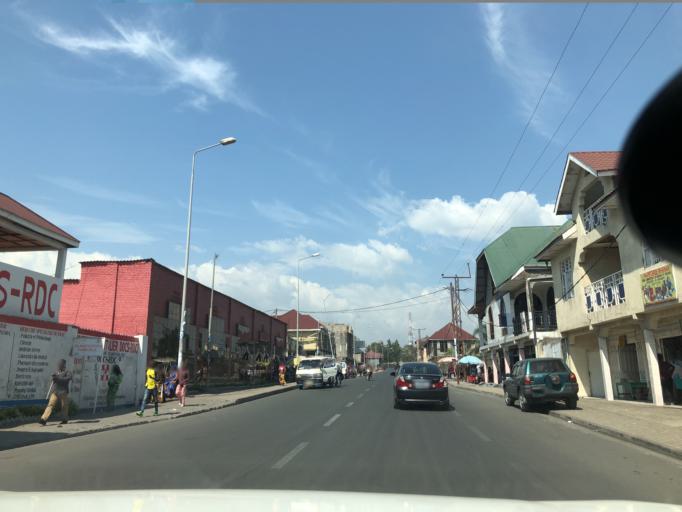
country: CD
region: Nord Kivu
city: Goma
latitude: -1.6609
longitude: 29.1867
